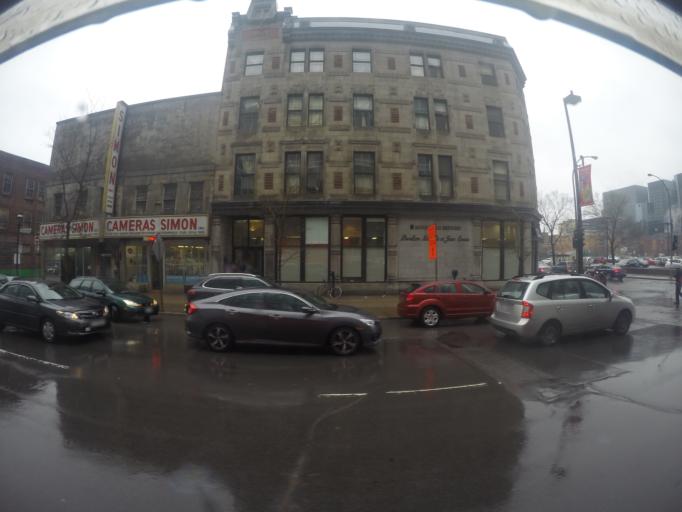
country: CA
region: Quebec
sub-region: Monteregie
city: Chateauguay
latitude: 45.3747
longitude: -73.6944
